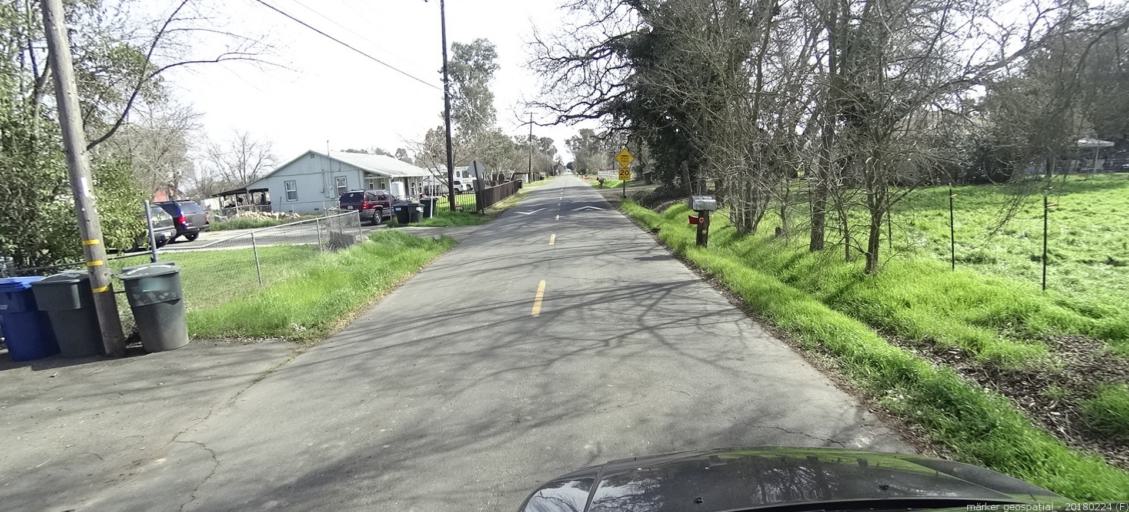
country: US
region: California
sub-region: Sacramento County
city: Rio Linda
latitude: 38.6728
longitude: -121.4365
